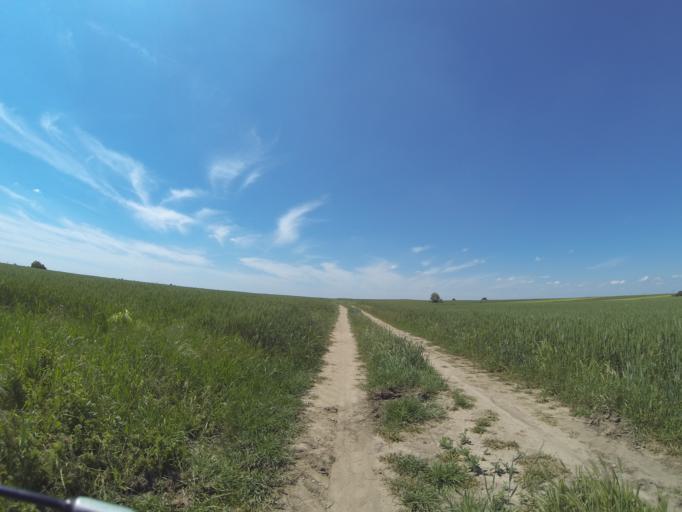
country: RO
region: Dolj
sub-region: Comuna Leu
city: Leu
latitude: 44.2143
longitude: 24.0248
